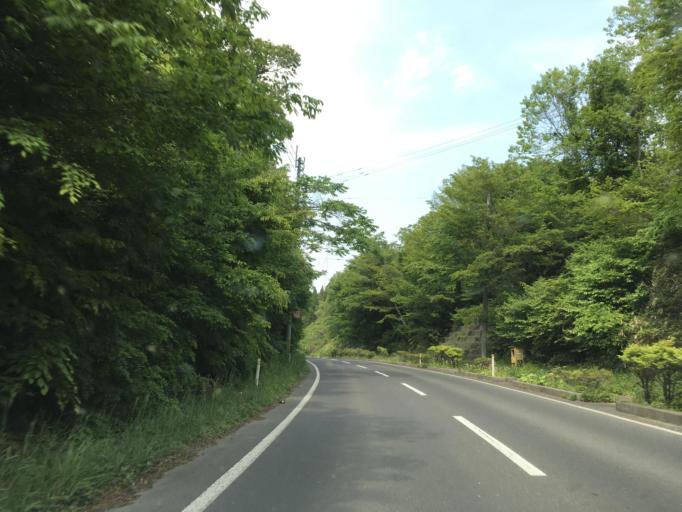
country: JP
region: Iwate
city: Ofunato
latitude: 38.8674
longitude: 141.5347
